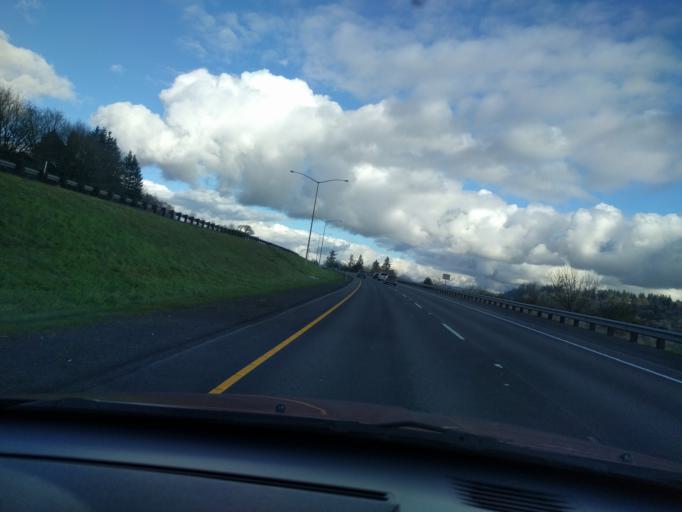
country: US
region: Oregon
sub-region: Clackamas County
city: West Linn
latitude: 45.3496
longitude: -122.6333
